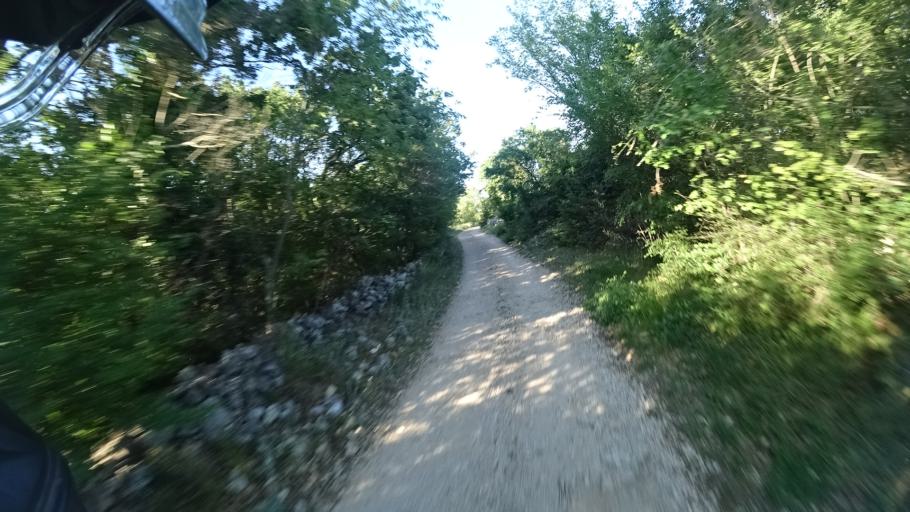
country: HR
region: Sibensko-Kniniska
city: Drnis
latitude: 43.8421
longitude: 16.0301
